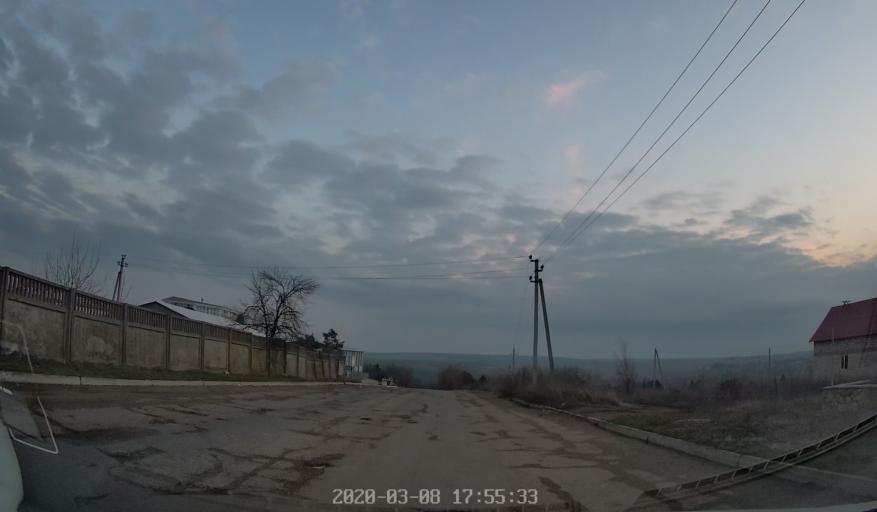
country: MD
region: Rezina
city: Rezina
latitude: 47.7512
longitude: 28.9490
